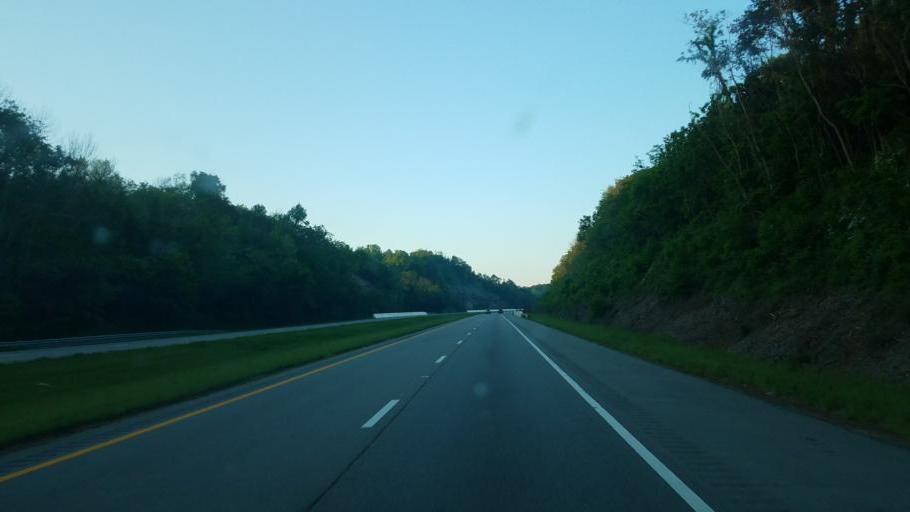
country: US
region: Ohio
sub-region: Washington County
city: Devola
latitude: 39.6152
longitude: -81.4584
